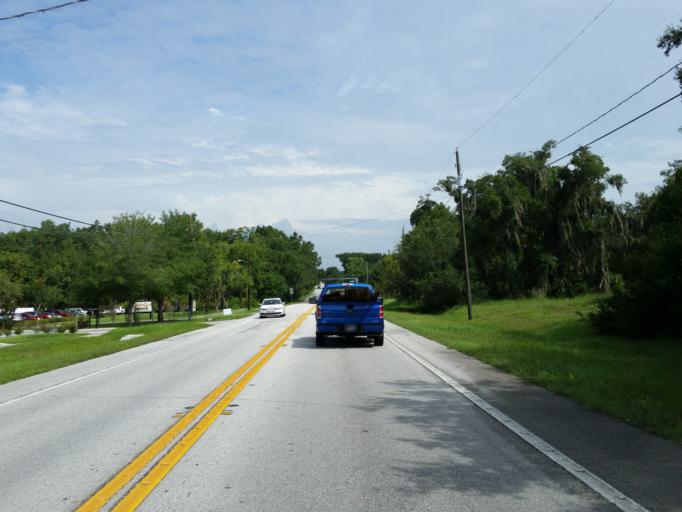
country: US
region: Florida
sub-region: Hillsborough County
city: Bloomingdale
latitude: 27.9015
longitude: -82.2507
